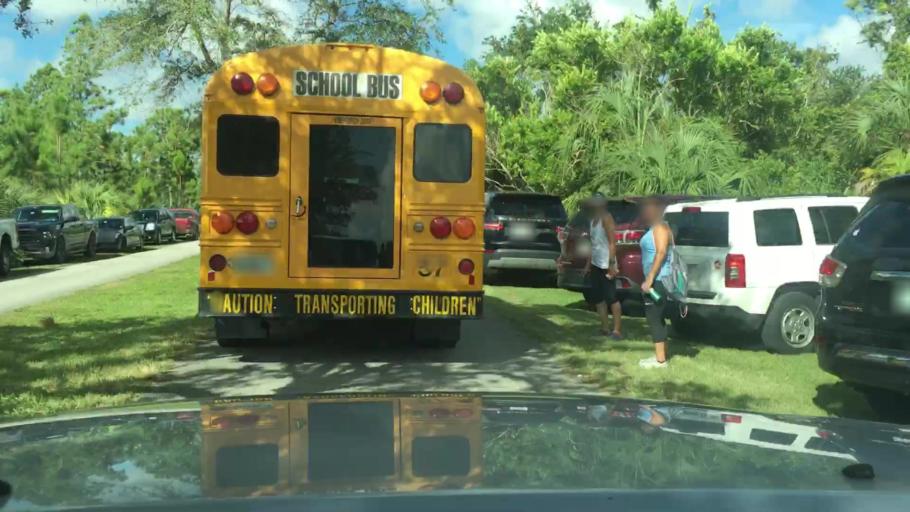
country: US
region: Florida
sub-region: Miami-Dade County
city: South Miami Heights
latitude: 25.5987
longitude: -80.4021
